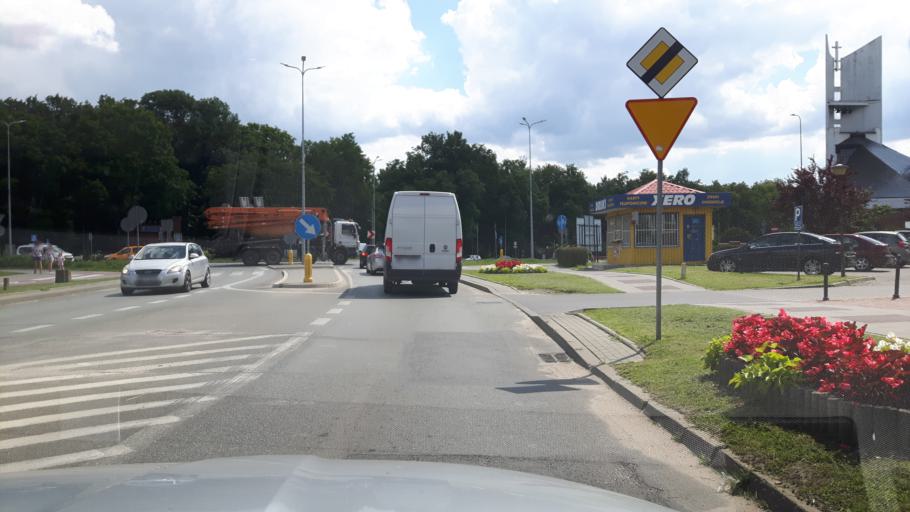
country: PL
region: Masovian Voivodeship
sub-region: Powiat wyszkowski
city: Wyszkow
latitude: 52.5927
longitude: 21.4527
